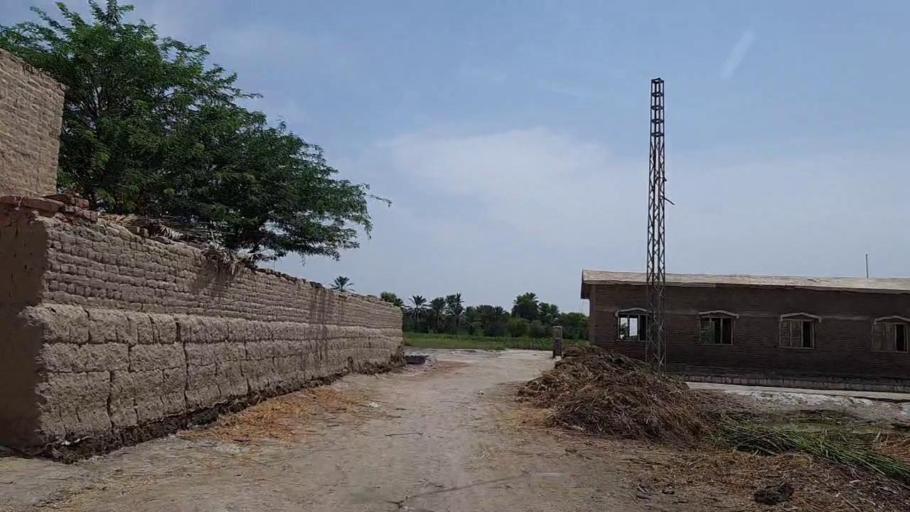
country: PK
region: Sindh
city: Khanpur
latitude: 27.7911
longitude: 69.4566
